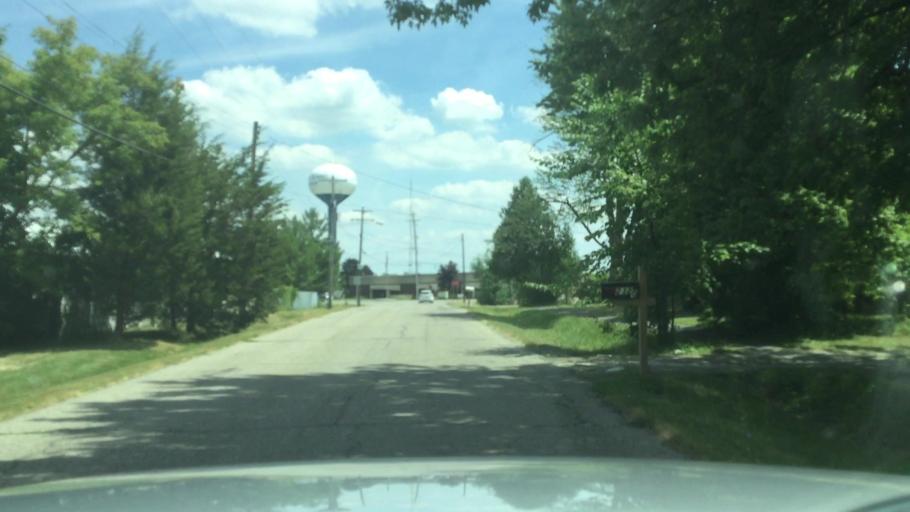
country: US
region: Michigan
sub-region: Genesee County
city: Grand Blanc
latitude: 42.9524
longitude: -83.6609
